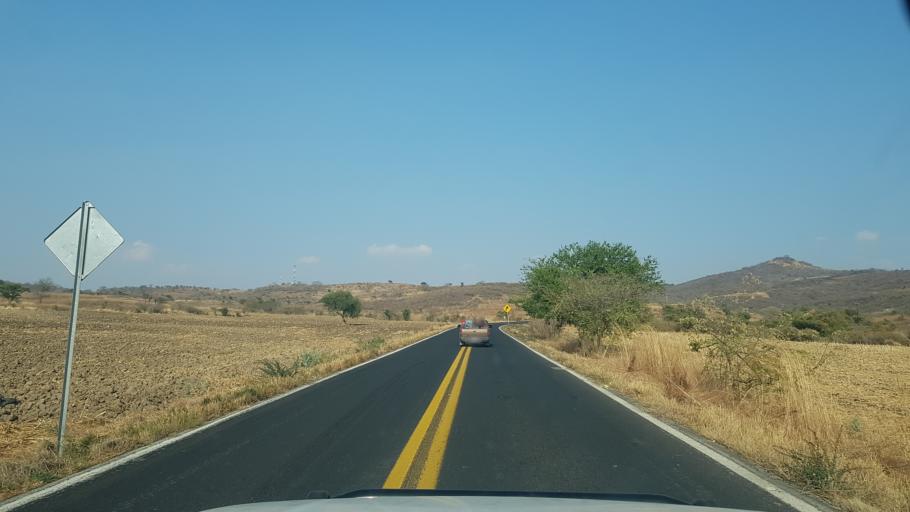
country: MX
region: Puebla
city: Calmeca
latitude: 18.6417
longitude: -98.6171
